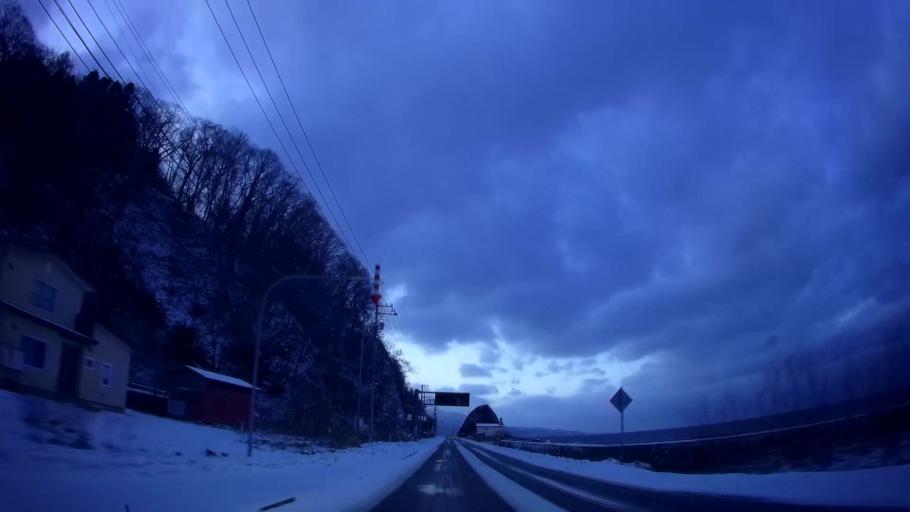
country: JP
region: Hokkaido
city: Hakodate
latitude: 41.8920
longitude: 141.0491
